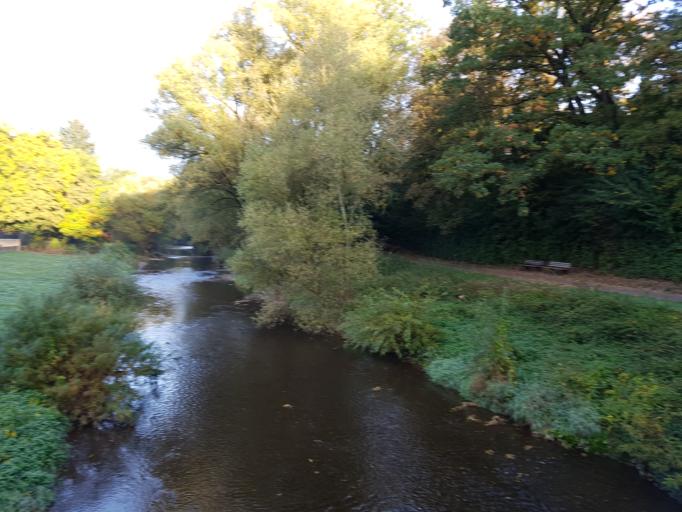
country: DE
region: Rheinland-Pfalz
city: Wittlich
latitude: 49.9805
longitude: 6.8939
